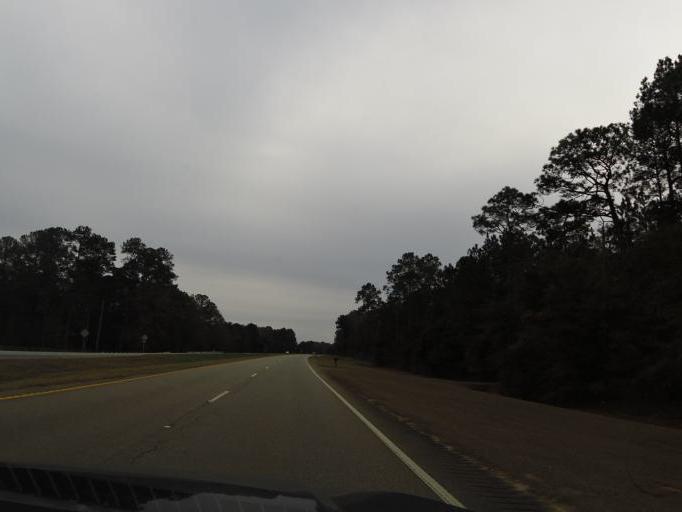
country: US
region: Georgia
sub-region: Thomas County
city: Thomasville
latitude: 30.7428
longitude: -83.9054
